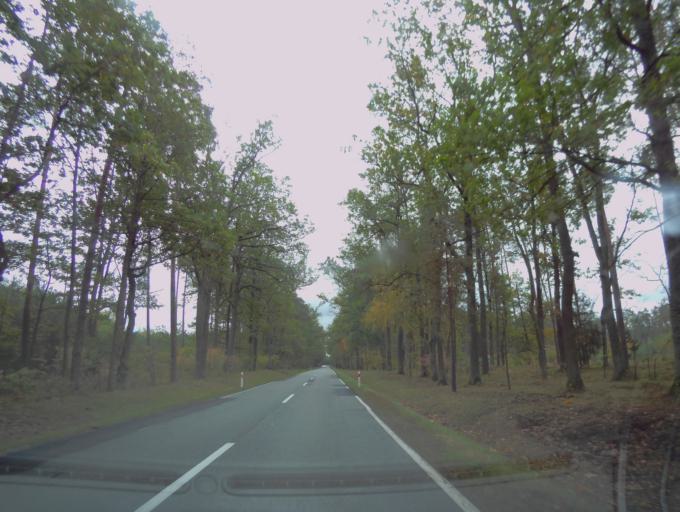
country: PL
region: Subcarpathian Voivodeship
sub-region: Powiat nizanski
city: Krzeszow
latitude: 50.3907
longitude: 22.3032
